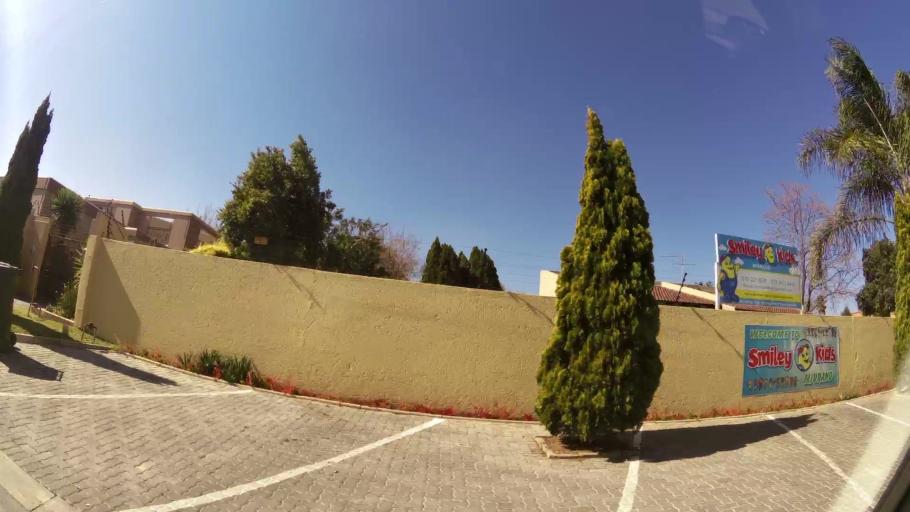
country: ZA
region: Gauteng
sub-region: City of Johannesburg Metropolitan Municipality
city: Midrand
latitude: -25.9609
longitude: 28.1272
